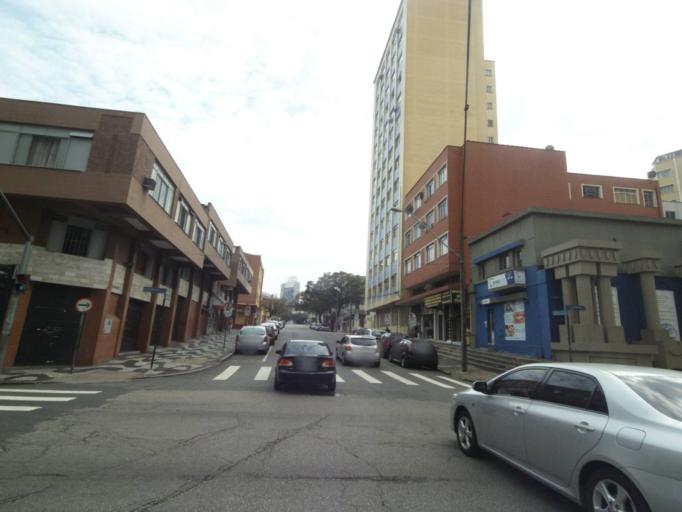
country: BR
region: Parana
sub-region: Curitiba
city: Curitiba
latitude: -25.4312
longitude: -49.2774
